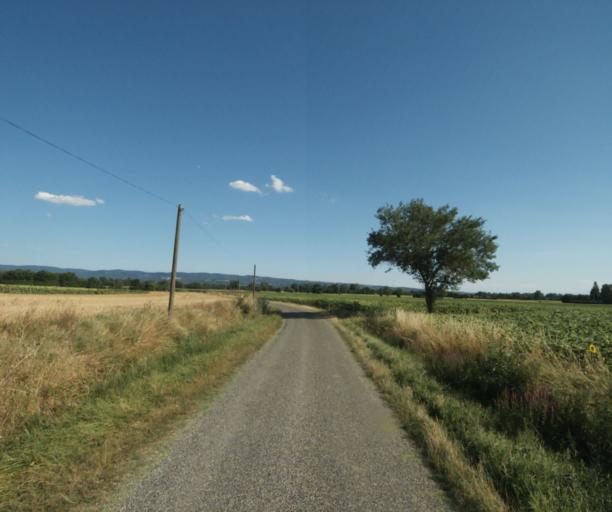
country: FR
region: Midi-Pyrenees
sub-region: Departement de la Haute-Garonne
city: Revel
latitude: 43.4881
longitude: 1.9470
